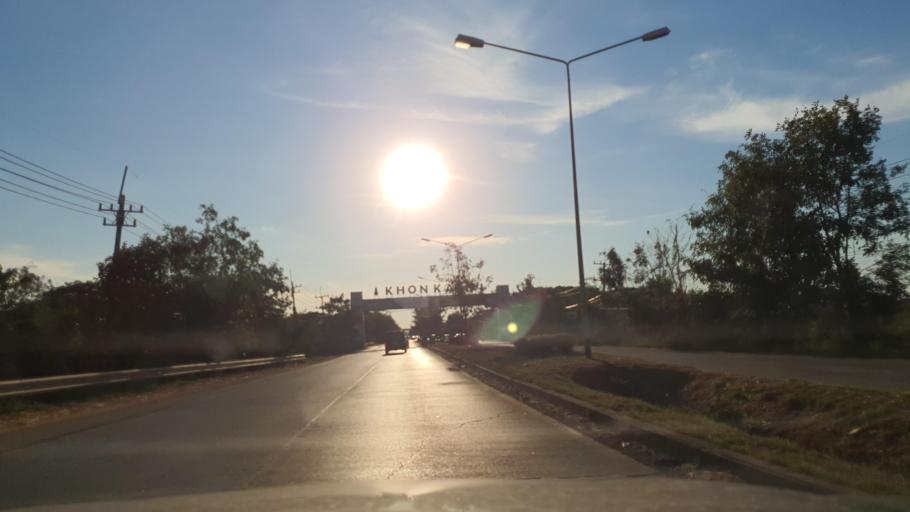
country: TH
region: Khon Kaen
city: Khon Kaen
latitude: 16.4349
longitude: 102.8968
